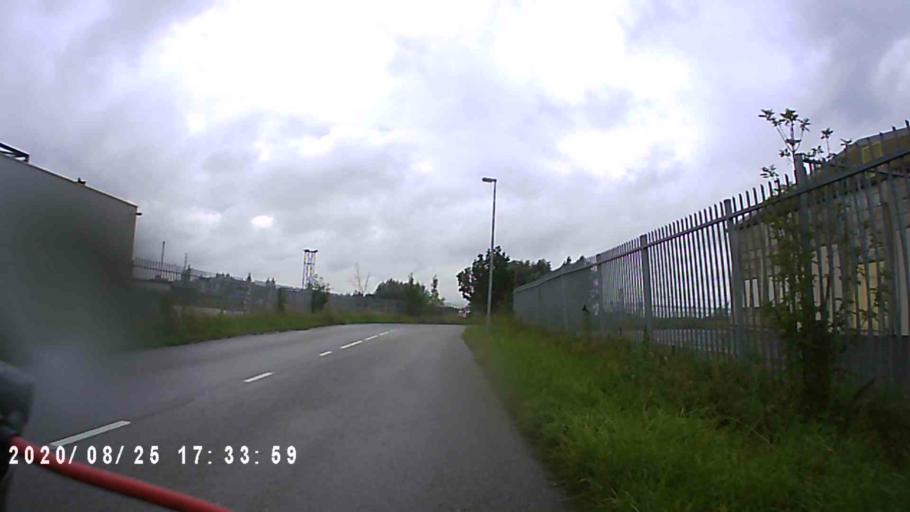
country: NL
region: Groningen
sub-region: Gemeente Zuidhorn
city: Aduard
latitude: 53.2146
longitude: 6.4862
